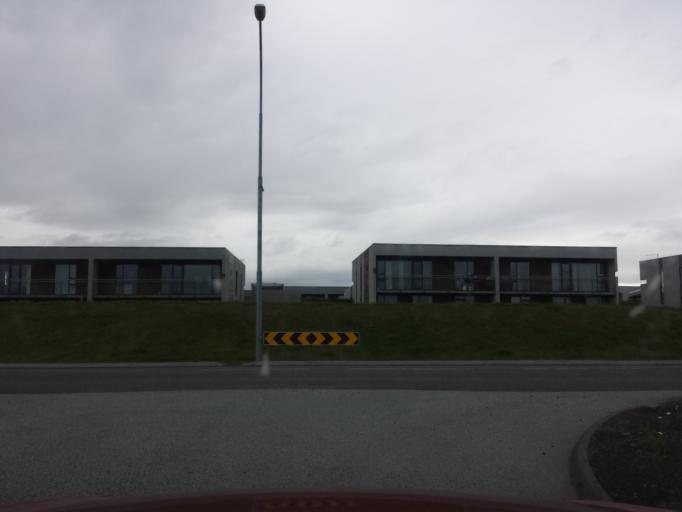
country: IS
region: Capital Region
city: Alftanes
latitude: 64.1010
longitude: -22.0169
